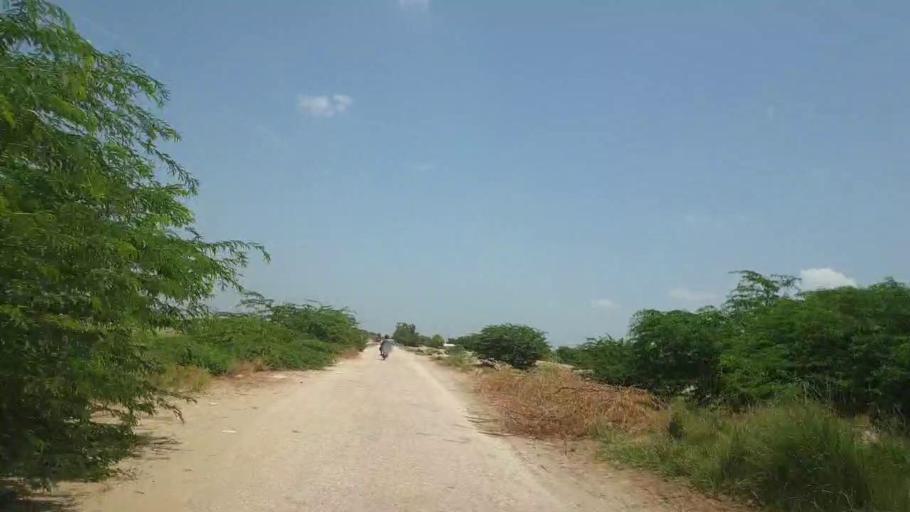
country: PK
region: Sindh
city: Pano Aqil
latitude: 27.6697
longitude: 69.2332
